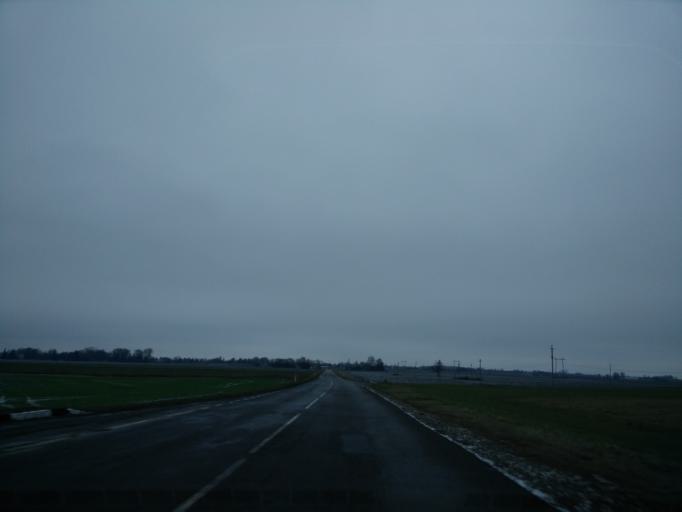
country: LT
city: Ariogala
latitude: 55.3147
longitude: 23.4318
